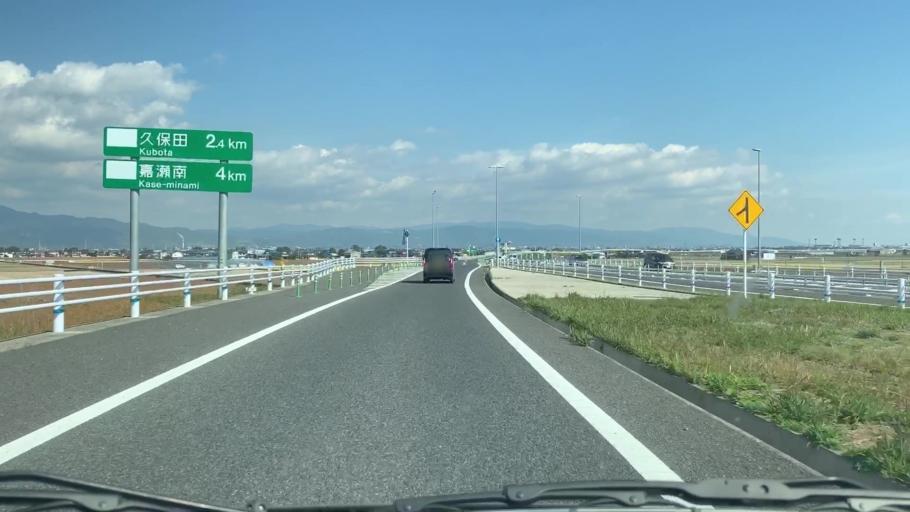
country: JP
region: Saga Prefecture
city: Saga-shi
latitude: 33.2225
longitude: 130.2154
